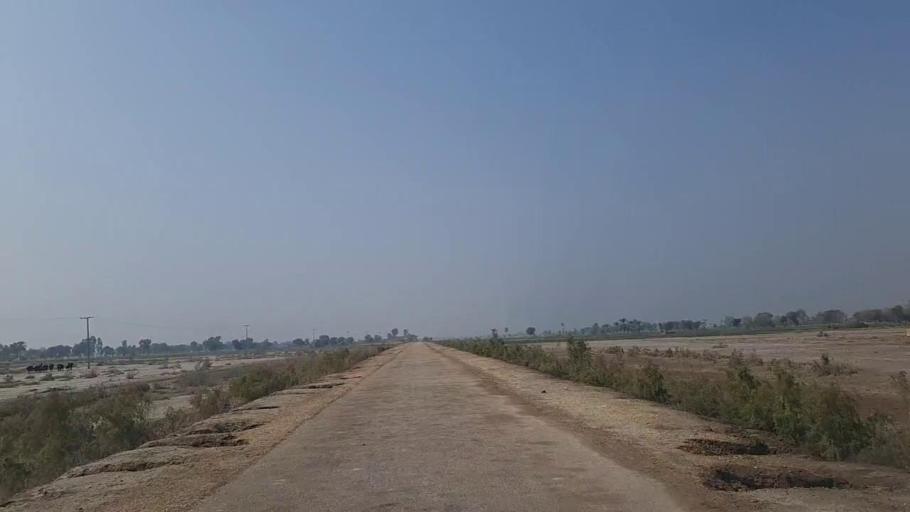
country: PK
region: Sindh
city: Nawabshah
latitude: 26.3600
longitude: 68.4288
